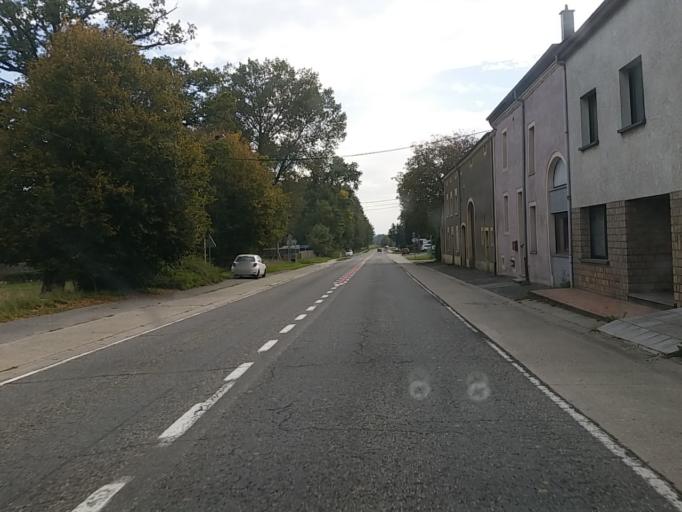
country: BE
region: Wallonia
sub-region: Province du Luxembourg
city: Etalle
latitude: 49.6747
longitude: 5.5641
